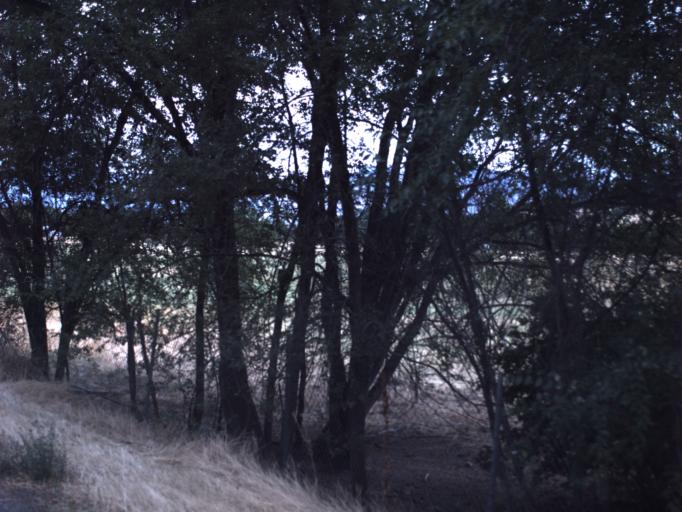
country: US
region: Utah
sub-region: Weber County
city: Riverdale
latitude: 41.1595
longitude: -112.0040
